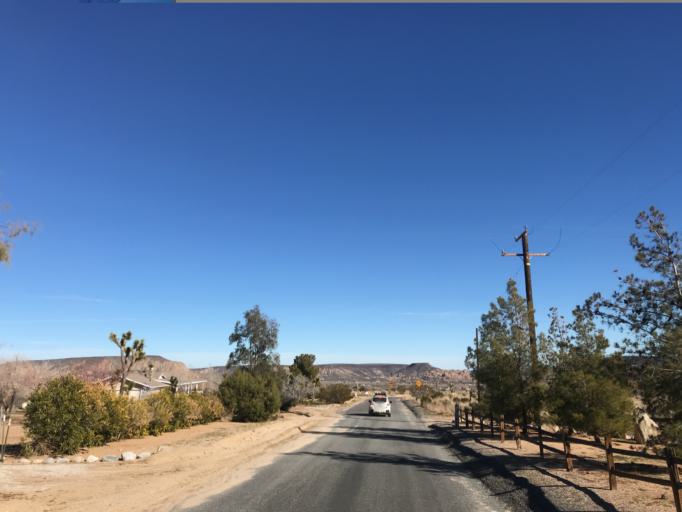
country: US
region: California
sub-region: San Bernardino County
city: Yucca Valley
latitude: 34.1981
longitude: -116.5479
